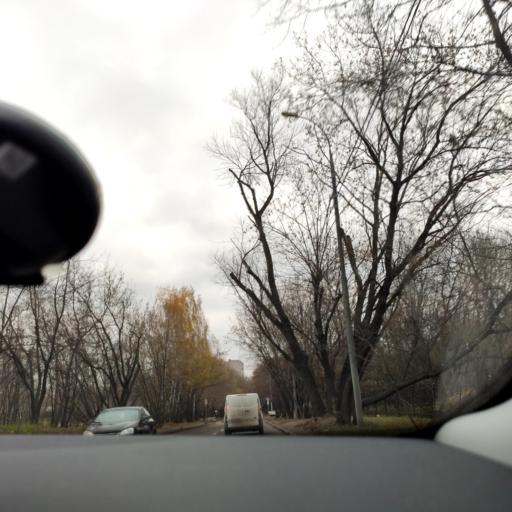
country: RU
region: Moscow
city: Kuz'minki
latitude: 55.6697
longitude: 37.8075
